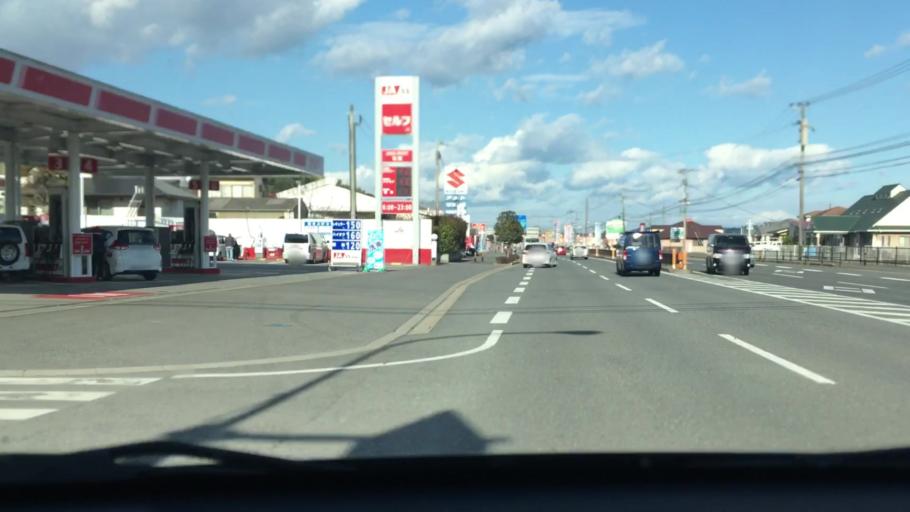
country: JP
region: Oita
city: Tsurusaki
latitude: 33.1883
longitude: 131.6705
